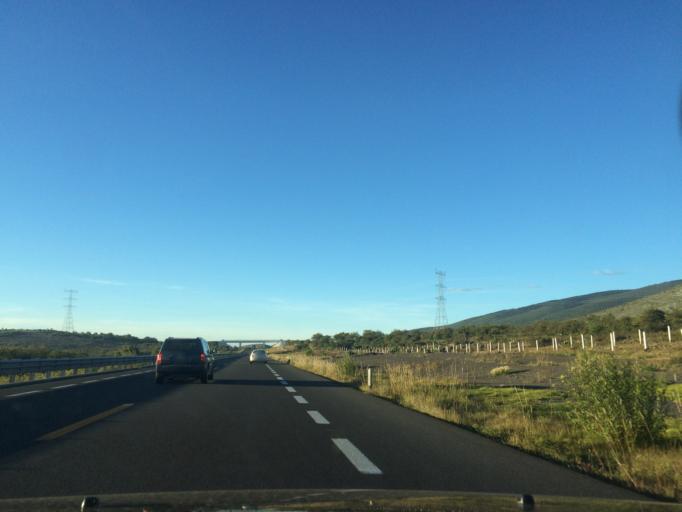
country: MX
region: Puebla
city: Morelos Canada
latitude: 18.7075
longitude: -97.4681
